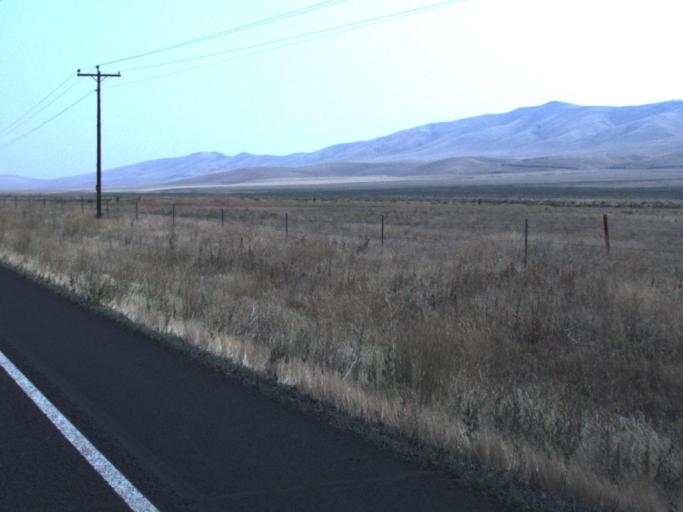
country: US
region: Washington
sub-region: Yakima County
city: Sunnyside
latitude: 46.5114
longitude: -120.0580
